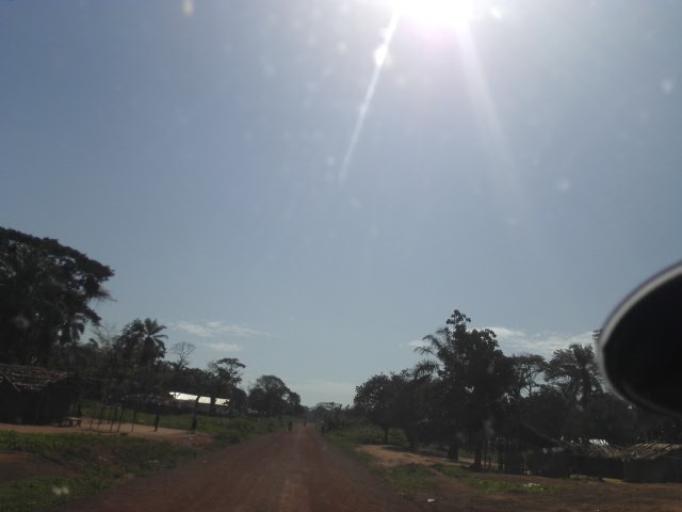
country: CD
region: Eastern Province
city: Wamba
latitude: 1.4095
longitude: 28.0842
